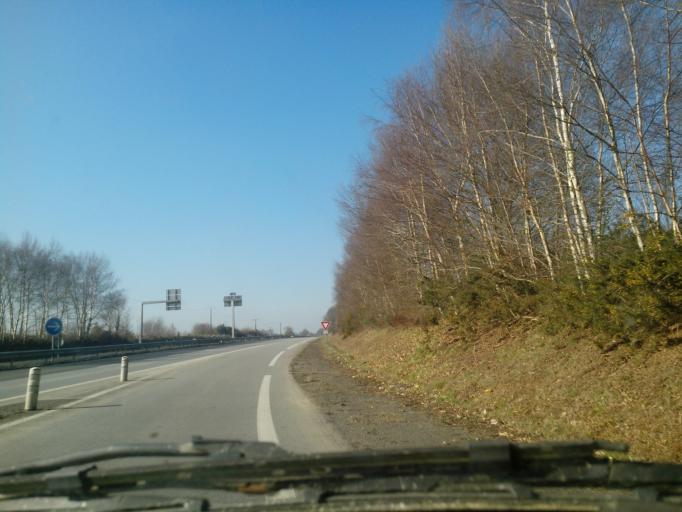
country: FR
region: Brittany
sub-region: Departement des Cotes-d'Armor
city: Merdrignac
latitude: 48.1882
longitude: -2.4264
